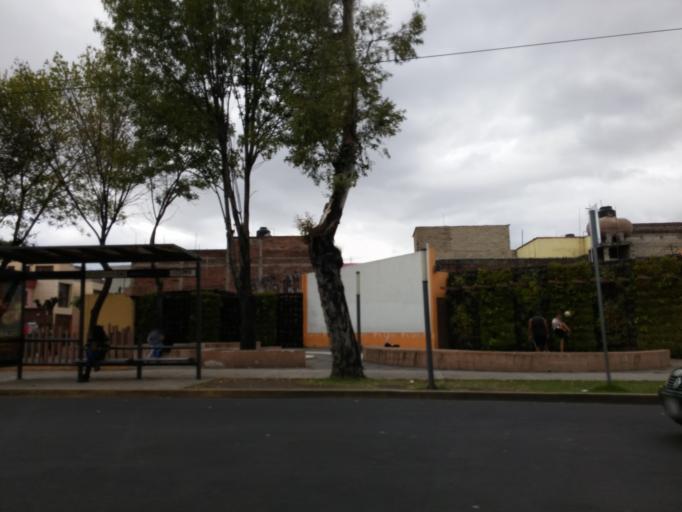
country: MX
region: Mexico City
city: Cuauhtemoc
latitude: 19.4607
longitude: -99.1697
